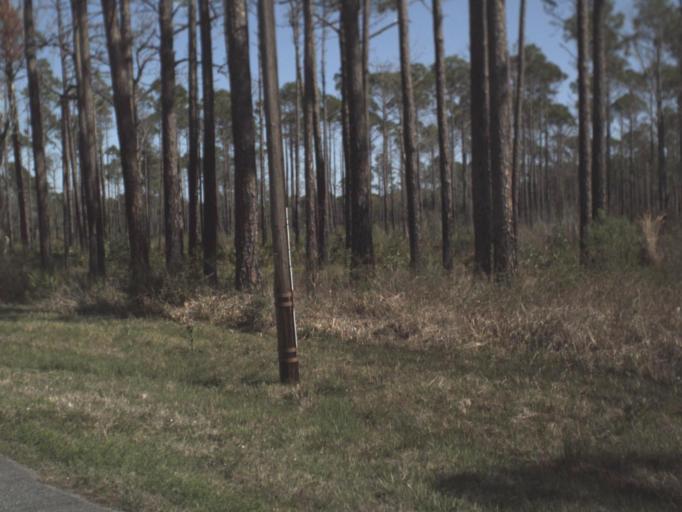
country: US
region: Florida
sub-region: Franklin County
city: Carrabelle
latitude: 29.9203
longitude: -84.4992
